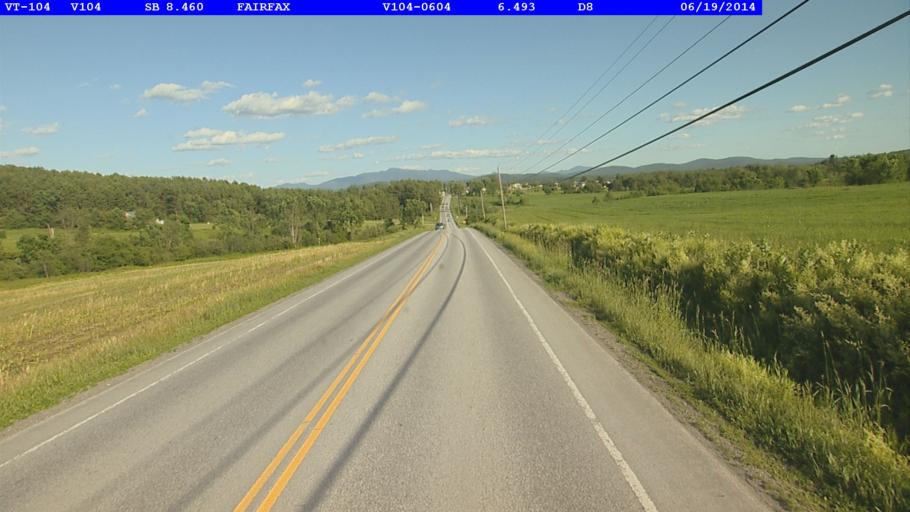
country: US
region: Vermont
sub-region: Chittenden County
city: Milton
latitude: 44.6796
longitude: -73.0261
